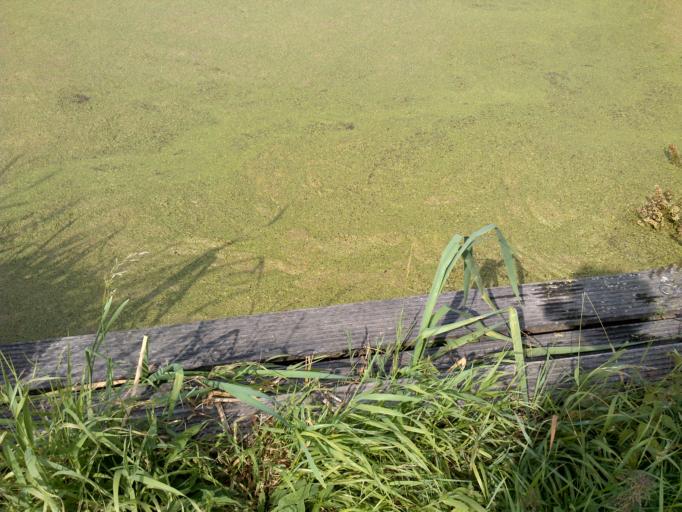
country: NL
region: South Holland
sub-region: Gemeente Delft
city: Delft
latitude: 51.9662
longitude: 4.3524
